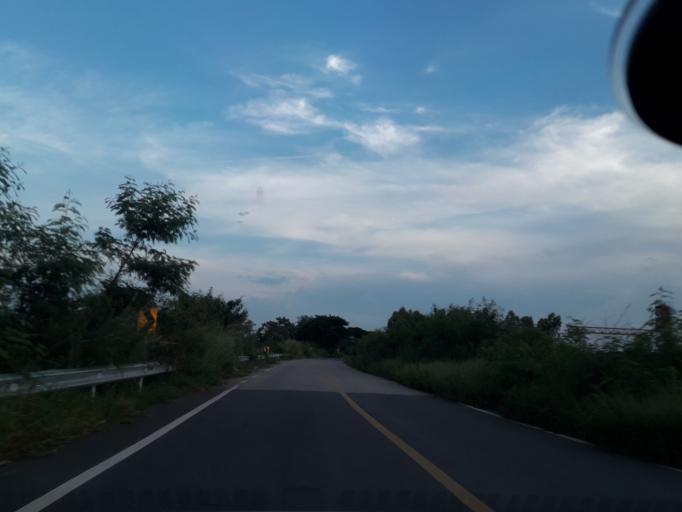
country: TH
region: Sara Buri
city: Nong Khae
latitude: 14.3008
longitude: 100.8900
